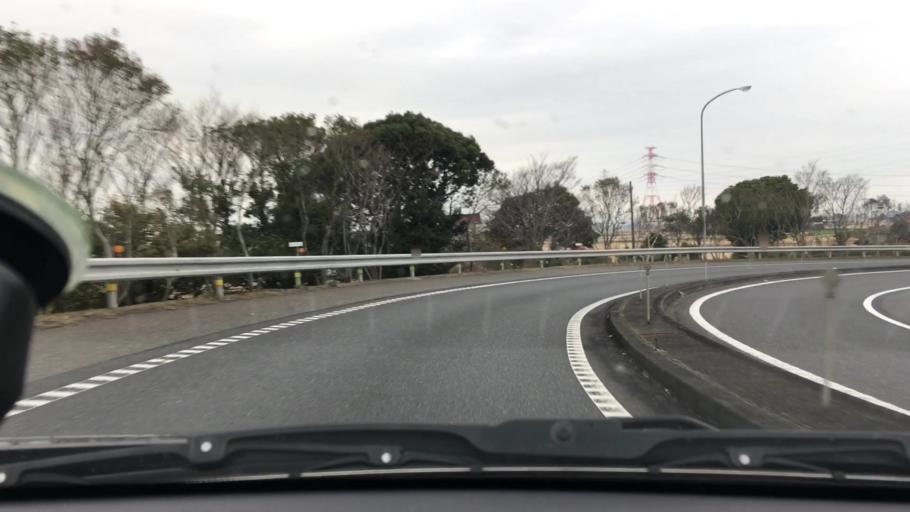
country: JP
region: Ibaraki
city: Itako
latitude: 35.9392
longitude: 140.5881
